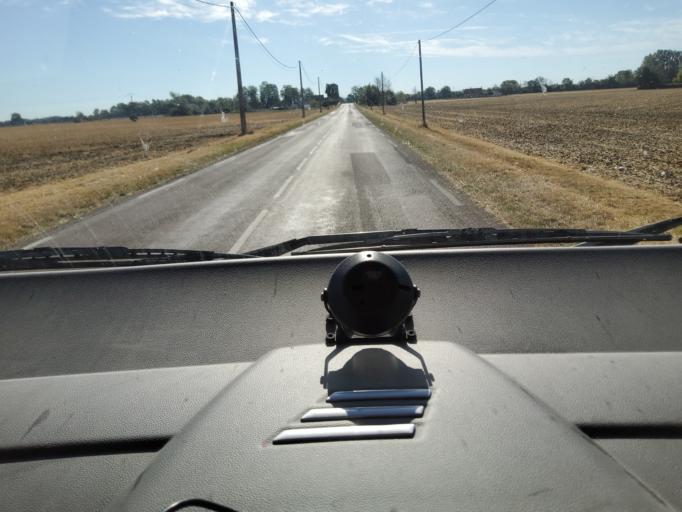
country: FR
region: Bourgogne
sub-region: Departement de la Cote-d'Or
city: Saint-Usage
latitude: 47.1482
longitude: 5.2785
